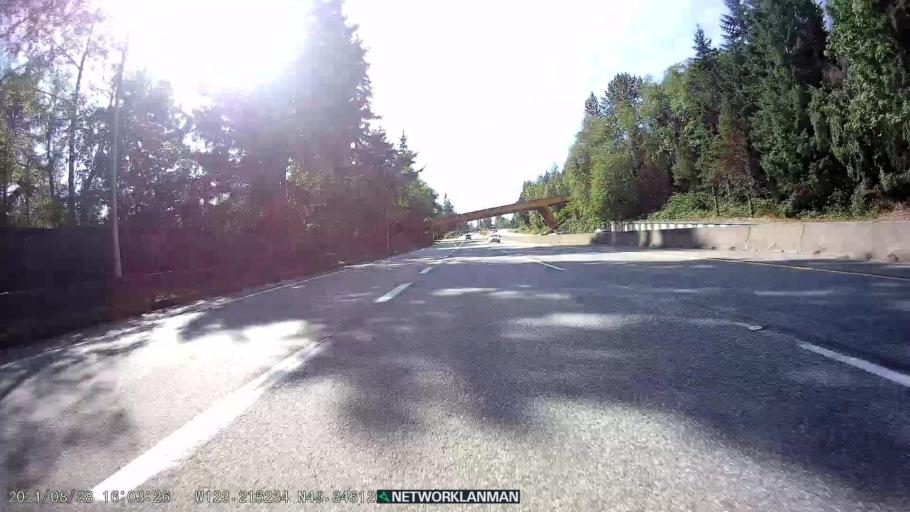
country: CA
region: British Columbia
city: West Vancouver
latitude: 49.3461
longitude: -123.2146
